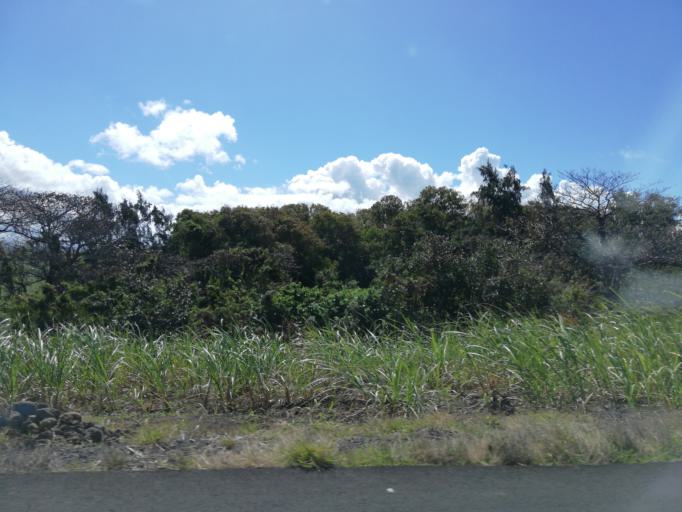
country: MU
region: Grand Port
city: Beau Vallon
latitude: -20.4475
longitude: 57.6980
